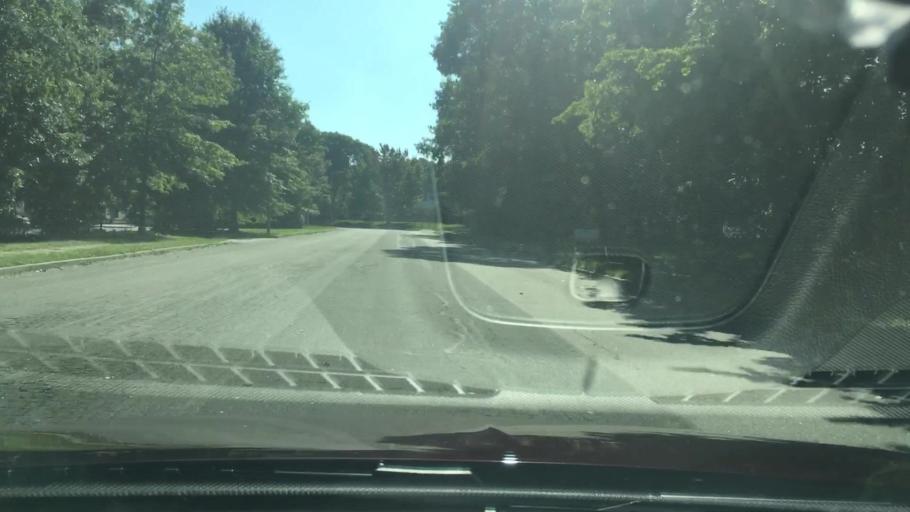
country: US
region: New York
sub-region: Suffolk County
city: Holtsville
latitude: 40.8028
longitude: -73.0398
